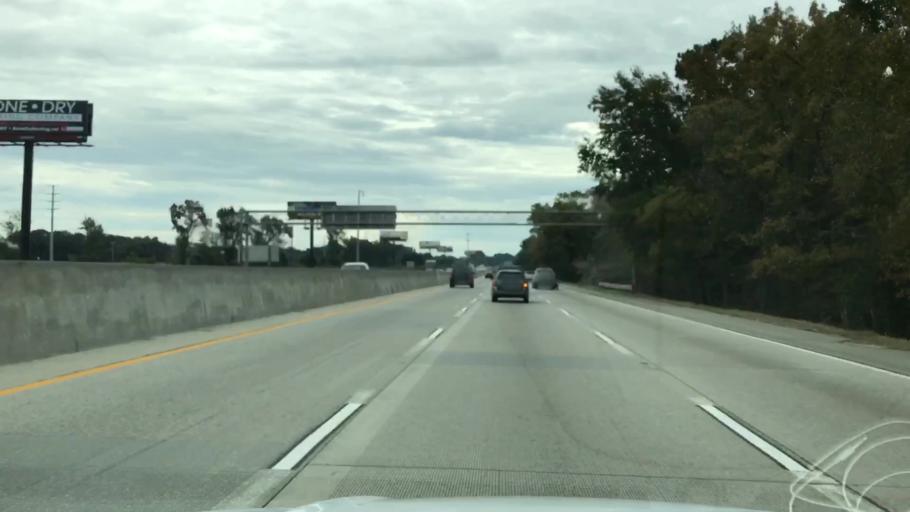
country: US
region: South Carolina
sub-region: Charleston County
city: North Charleston
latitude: 32.8625
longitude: -79.9956
